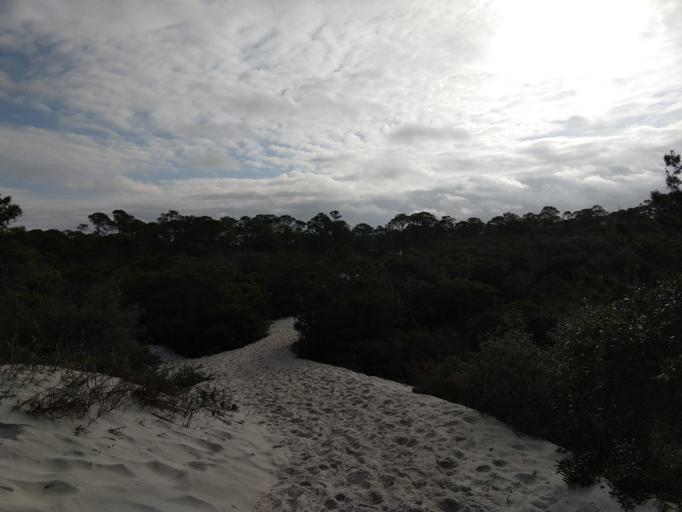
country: US
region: Florida
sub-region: Gulf County
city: Port Saint Joe
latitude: 29.7892
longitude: -85.4092
